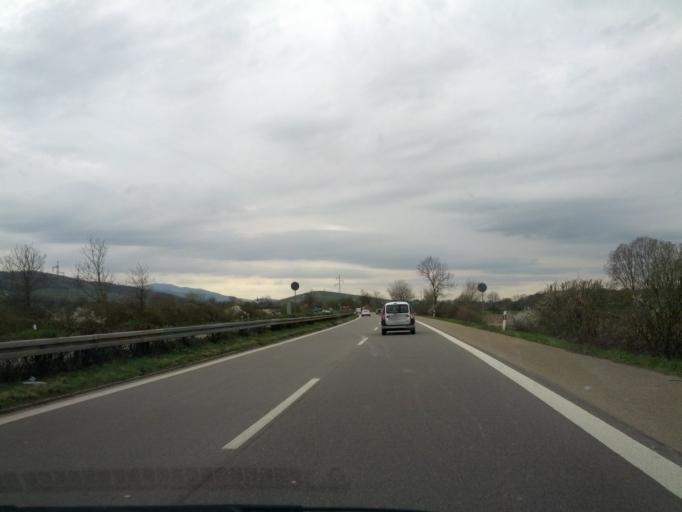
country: DE
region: Baden-Wuerttemberg
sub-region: Freiburg Region
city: Ebringen
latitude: 47.9781
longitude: 7.7746
